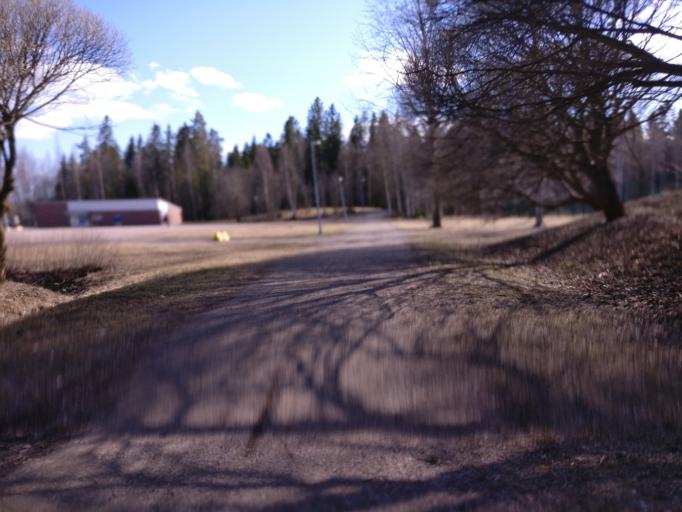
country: FI
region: Uusimaa
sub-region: Helsinki
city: Jaervenpaeae
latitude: 60.4949
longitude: 25.0762
